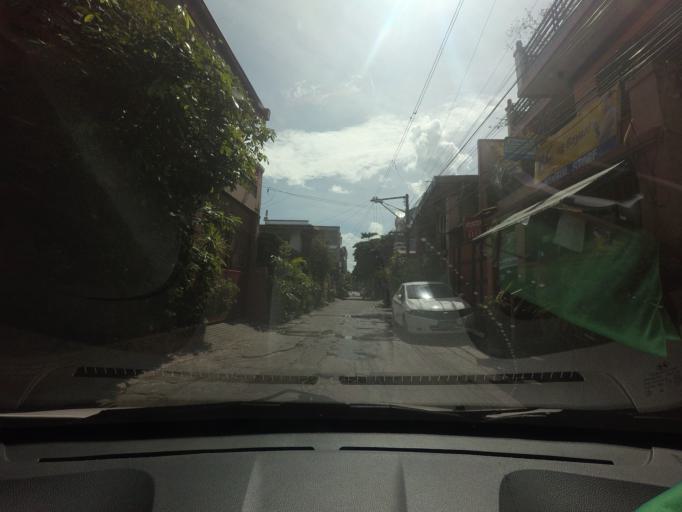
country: PH
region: Calabarzon
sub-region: Province of Rizal
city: Taguig
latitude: 14.5276
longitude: 121.0755
